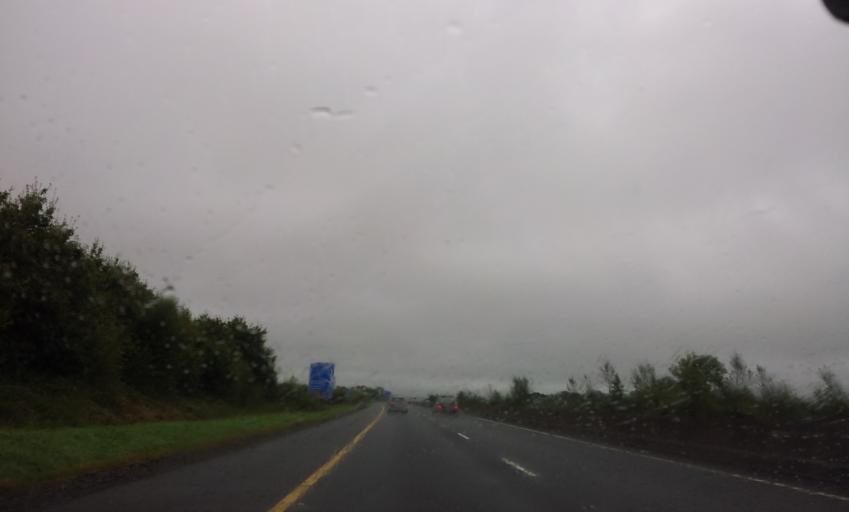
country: IE
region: Munster
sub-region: County Cork
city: Mitchelstown
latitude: 52.2744
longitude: -8.2341
